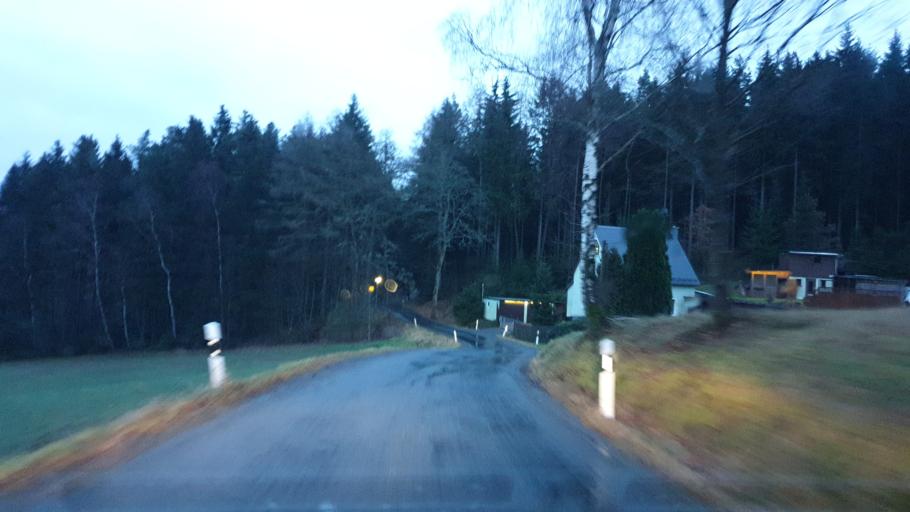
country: DE
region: Saxony
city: Bad Elster
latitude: 50.3060
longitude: 12.2380
